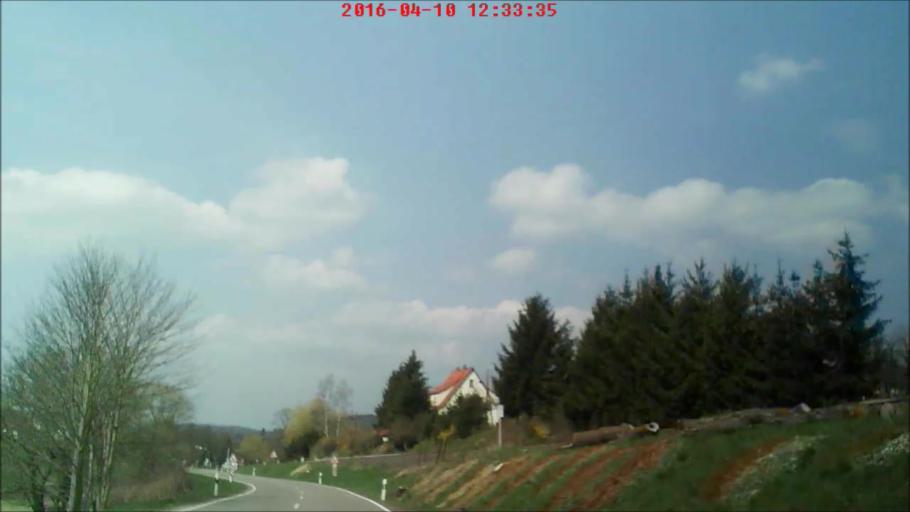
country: DE
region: Thuringia
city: Breitenbach
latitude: 50.7072
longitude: 10.4807
